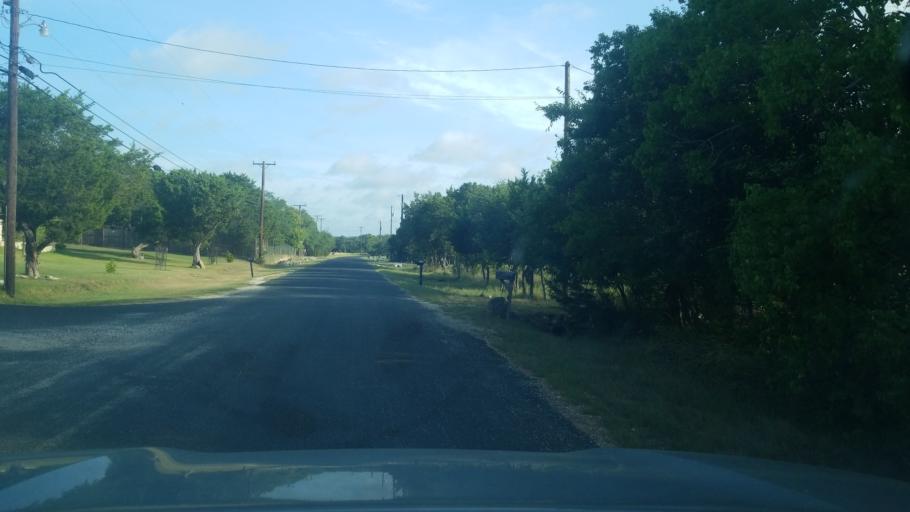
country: US
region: Texas
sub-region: Bexar County
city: Timberwood Park
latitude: 29.7012
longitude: -98.5122
